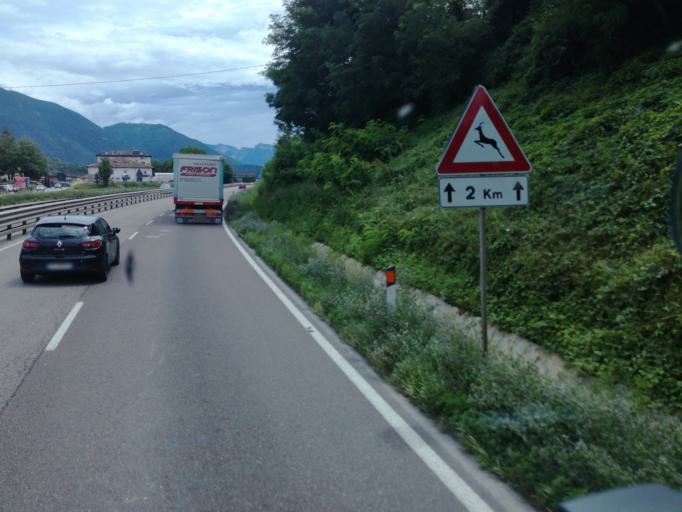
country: IT
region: Trentino-Alto Adige
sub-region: Provincia di Trento
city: Madrano-Canzolino
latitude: 46.0803
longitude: 11.2010
